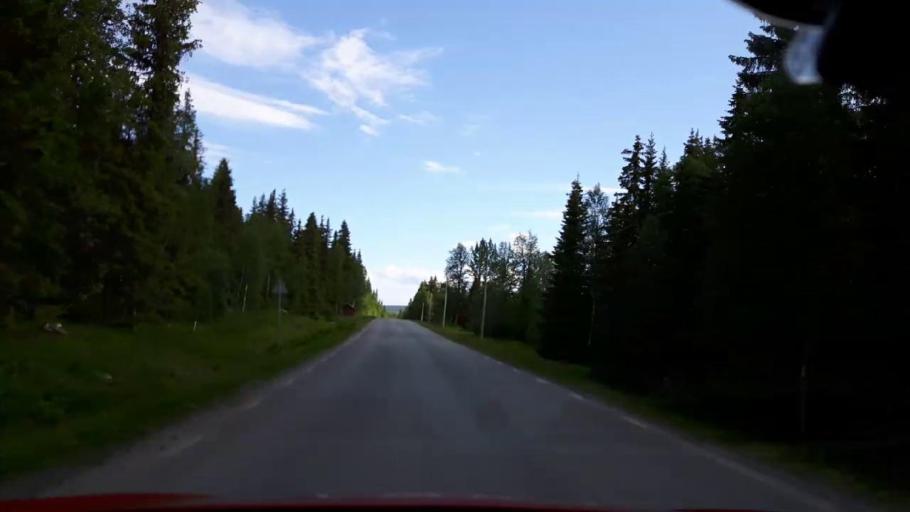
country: SE
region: Jaemtland
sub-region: Krokoms Kommun
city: Valla
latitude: 63.7776
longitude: 14.0435
